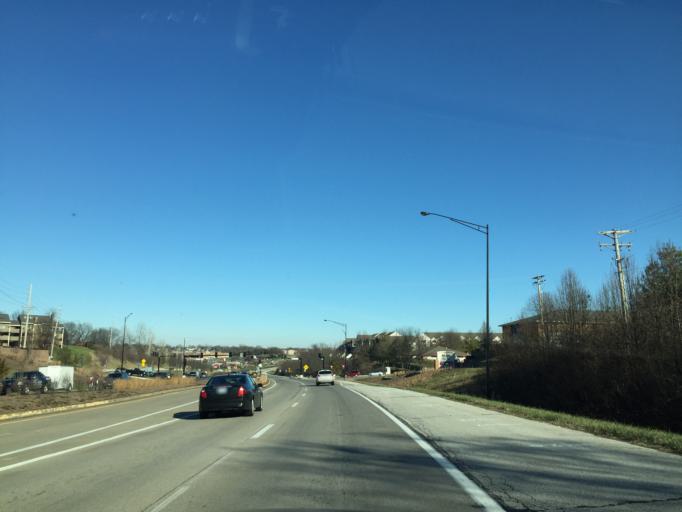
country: US
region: Missouri
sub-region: Saint Louis County
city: Ellisville
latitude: 38.5826
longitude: -90.6171
